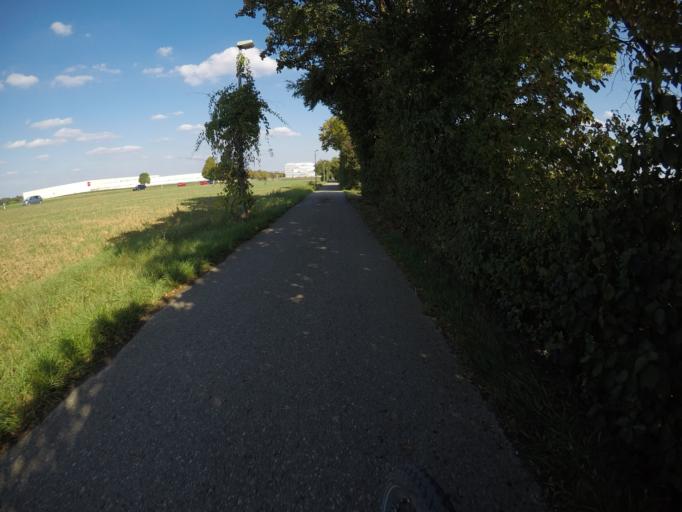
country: DE
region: Baden-Wuerttemberg
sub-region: Regierungsbezirk Stuttgart
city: Neuhausen auf den Fildern
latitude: 48.6815
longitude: 9.2473
